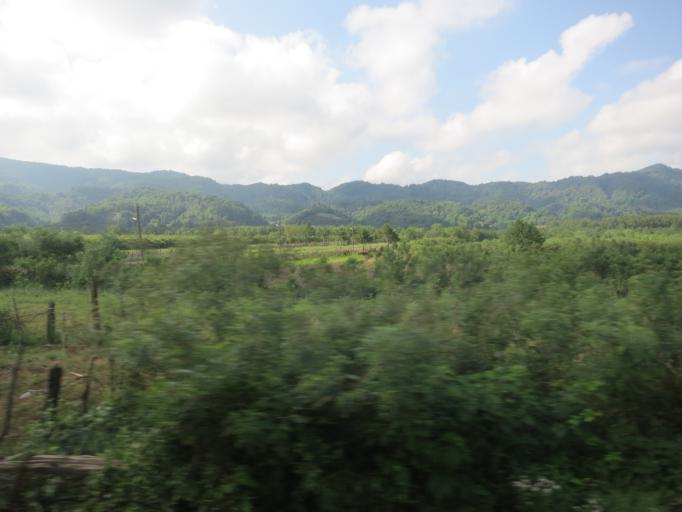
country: GE
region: Guria
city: Lanchkhuti
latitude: 42.0849
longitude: 42.0800
